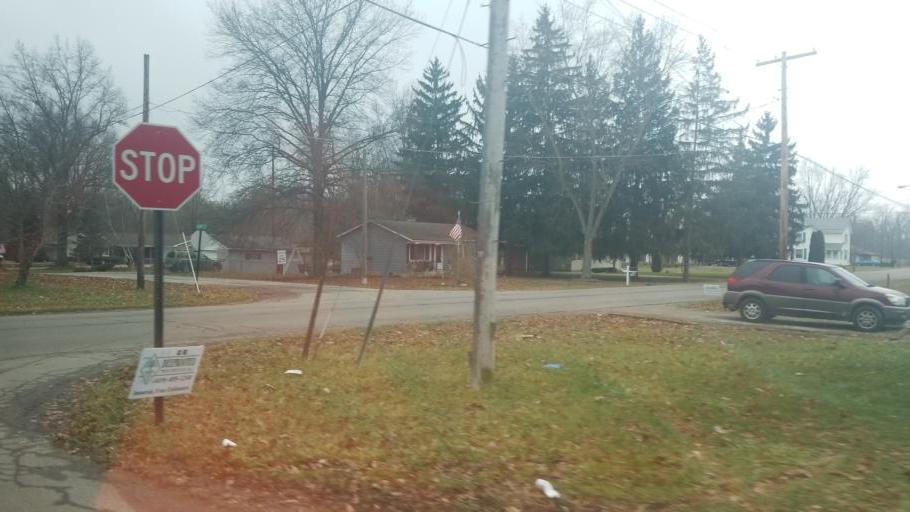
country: US
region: Ohio
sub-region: Crawford County
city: Galion
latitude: 40.7263
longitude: -82.7684
